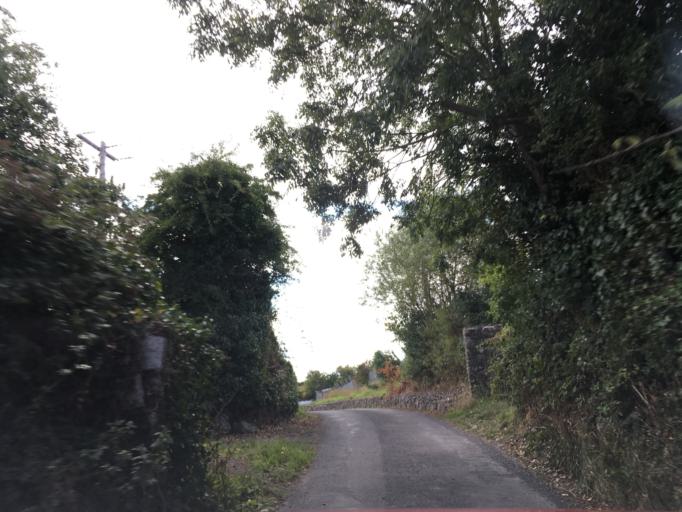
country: IE
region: Munster
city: Cashel
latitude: 52.5206
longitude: -7.8793
